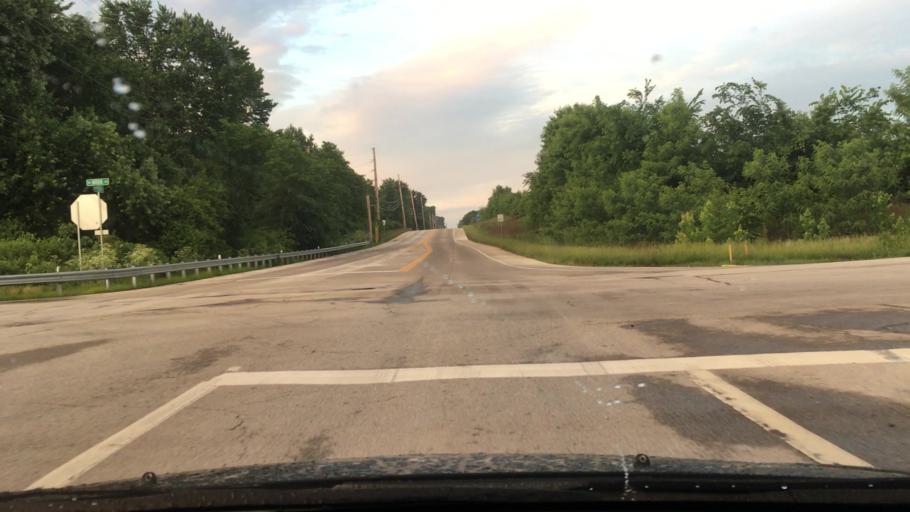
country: US
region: Missouri
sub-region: Jackson County
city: Lees Summit
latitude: 38.8685
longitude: -94.4164
